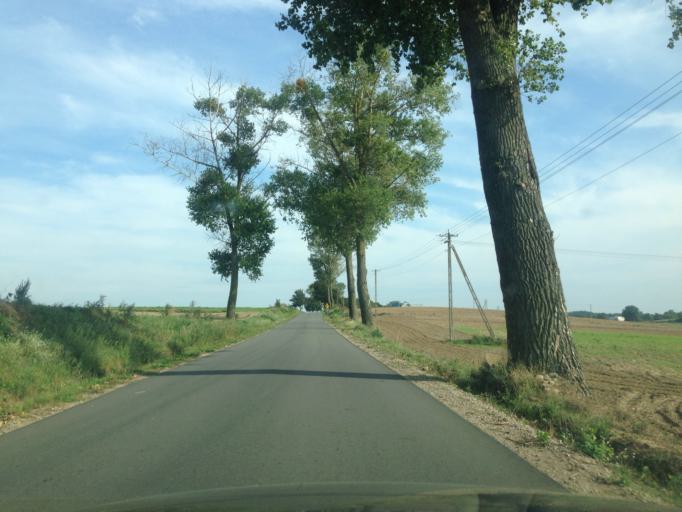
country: PL
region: Kujawsko-Pomorskie
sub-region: Powiat brodnicki
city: Bartniczka
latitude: 53.2543
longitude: 19.6517
